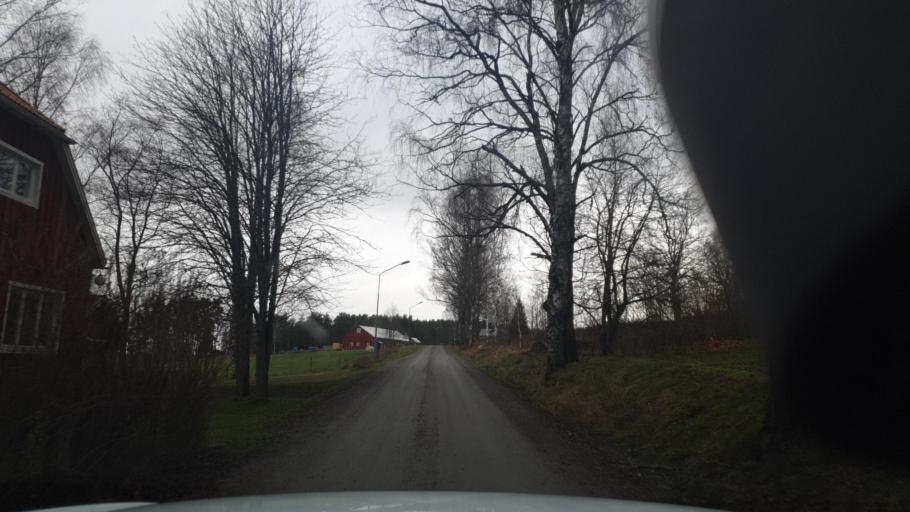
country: SE
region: Vaermland
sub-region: Karlstads Kommun
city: Edsvalla
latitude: 59.6120
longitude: 13.0680
